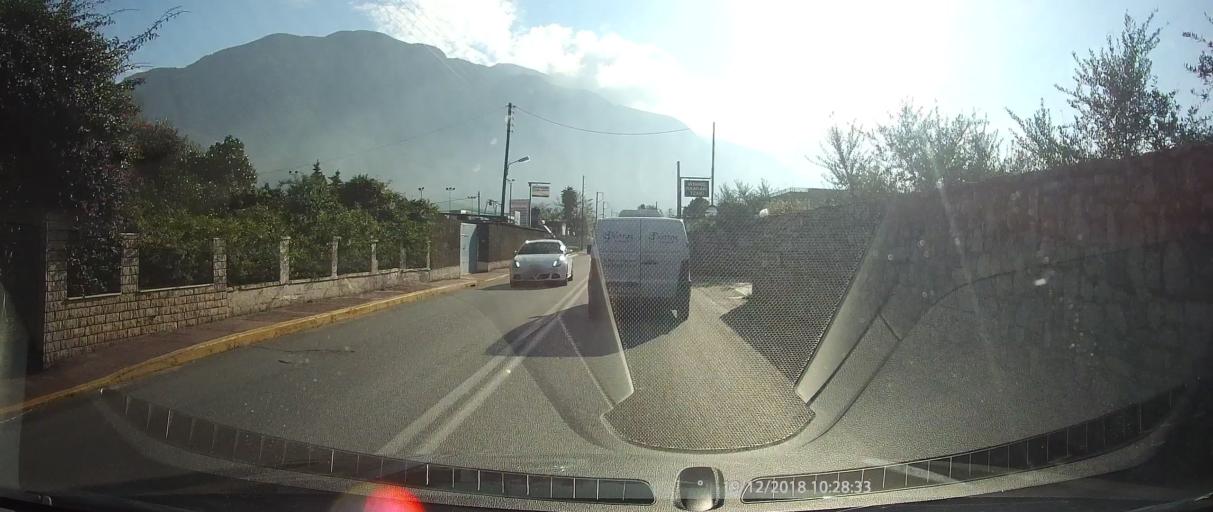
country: GR
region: Peloponnese
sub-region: Nomos Messinias
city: Paralia Vergas
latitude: 37.0276
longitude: 22.1416
